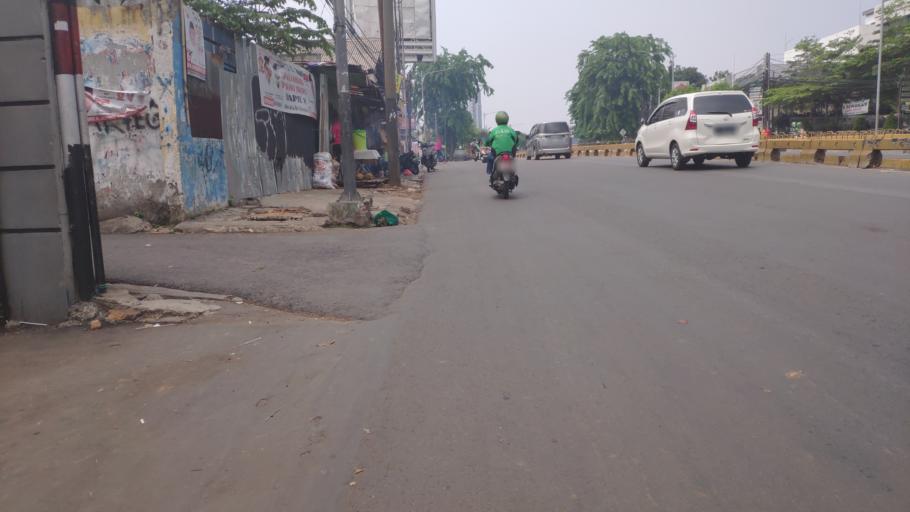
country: ID
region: Jakarta Raya
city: Jakarta
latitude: -6.2652
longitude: 106.8305
